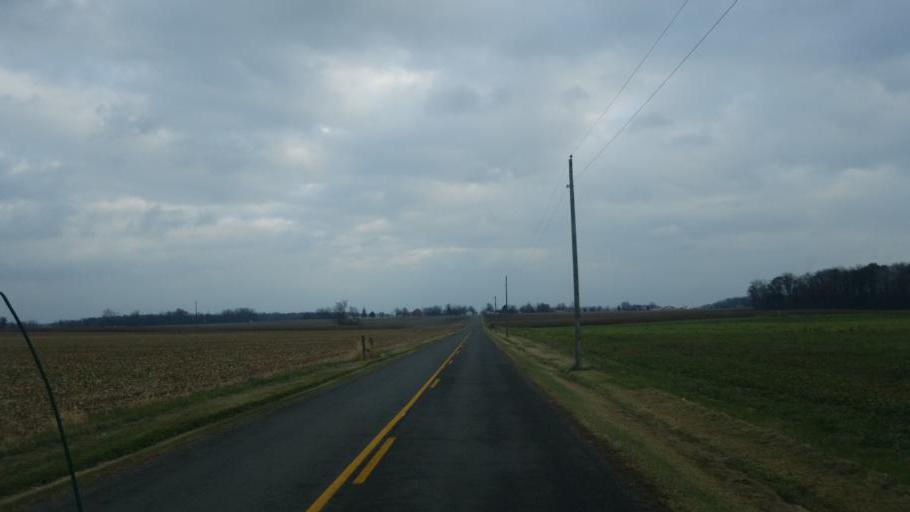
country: US
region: Ohio
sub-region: Mercer County
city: Coldwater
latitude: 40.5090
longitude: -84.7205
